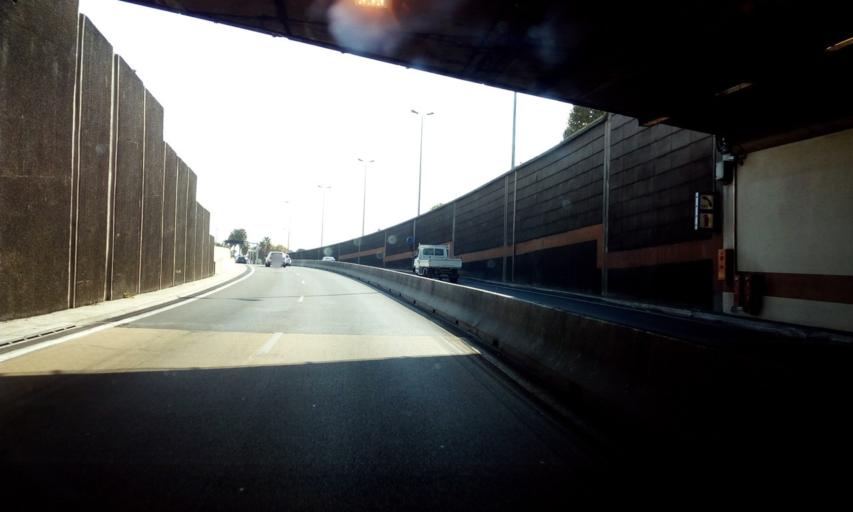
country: FR
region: Provence-Alpes-Cote d'Azur
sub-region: Departement du Var
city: Toulon
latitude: 43.1203
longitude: 5.9491
